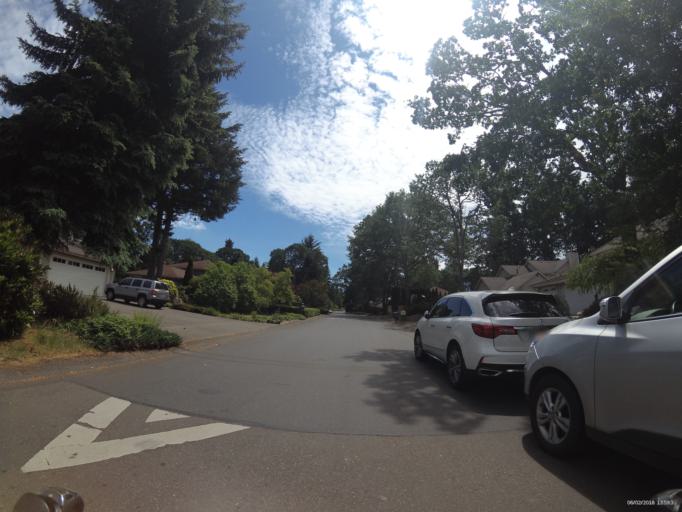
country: US
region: Washington
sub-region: Pierce County
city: University Place
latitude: 47.2077
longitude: -122.5644
